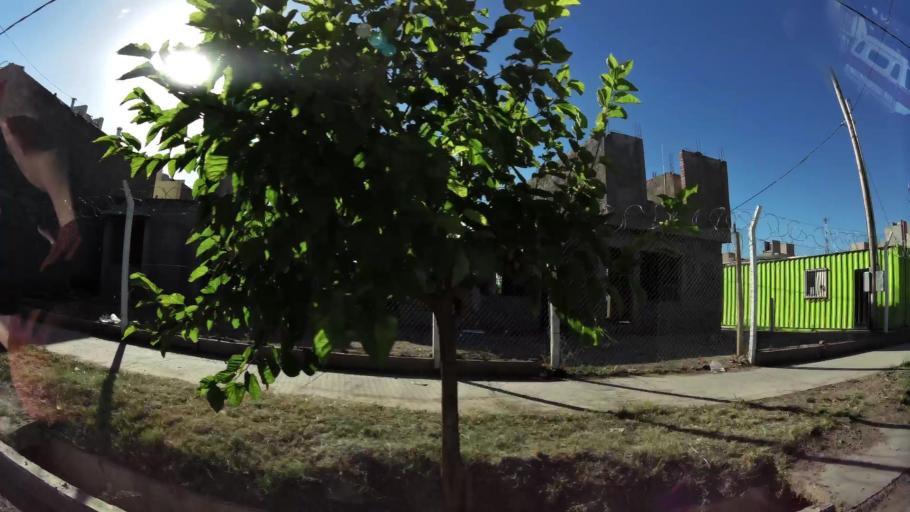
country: AR
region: Mendoza
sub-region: Departamento de Godoy Cruz
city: Godoy Cruz
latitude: -32.9343
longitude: -68.8316
